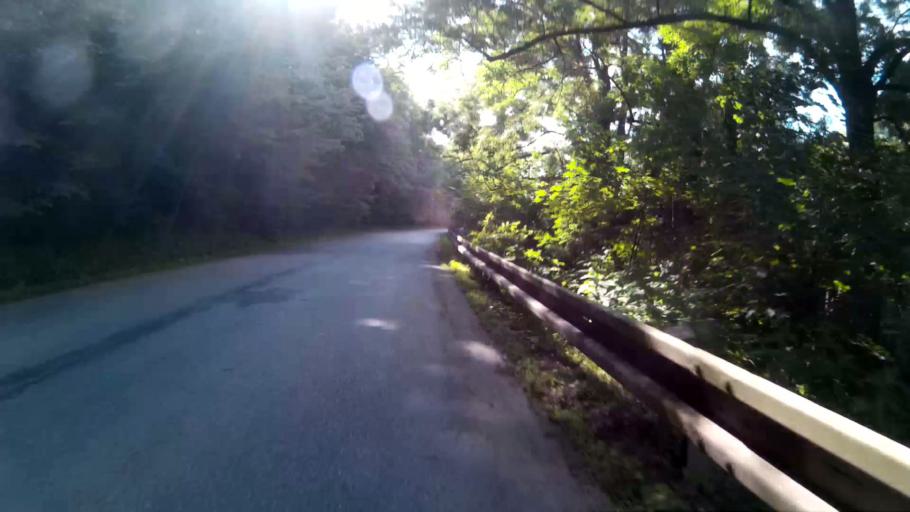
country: CZ
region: South Moravian
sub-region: Okres Brno-Venkov
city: Rosice
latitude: 49.1698
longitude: 16.4163
